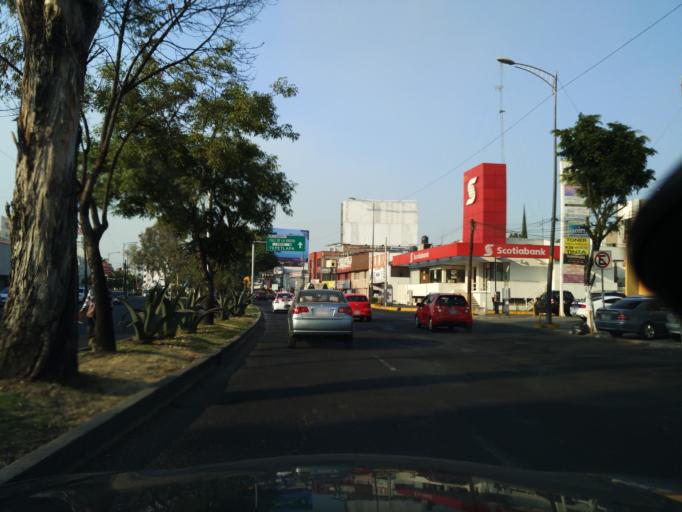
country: MX
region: Mexico City
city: Xochimilco
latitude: 19.3128
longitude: -99.1104
